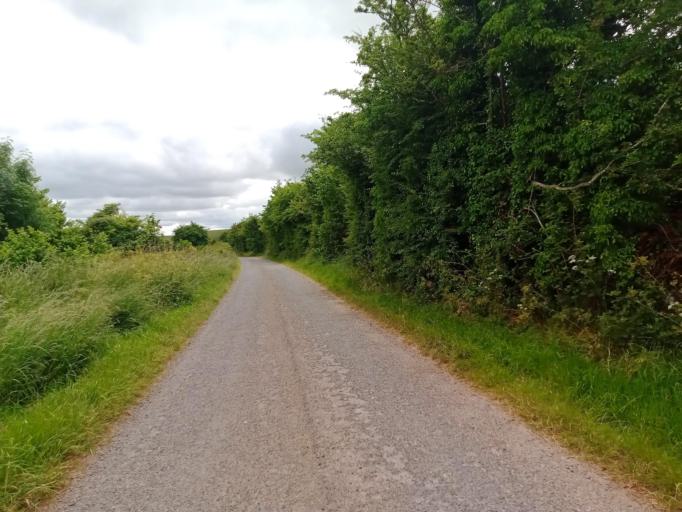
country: IE
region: Leinster
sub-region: Laois
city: Rathdowney
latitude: 52.7906
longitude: -7.4812
